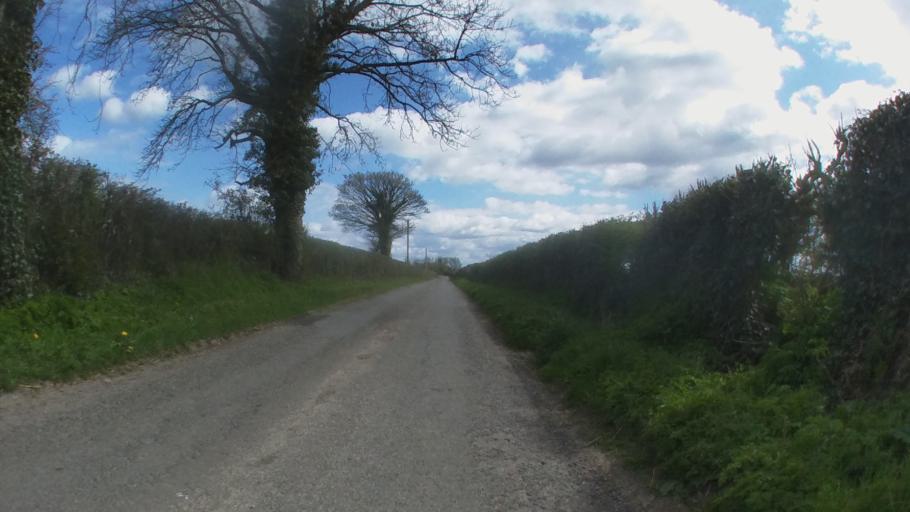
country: IE
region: Leinster
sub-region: Kilkenny
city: Kilkenny
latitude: 52.7083
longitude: -7.2145
